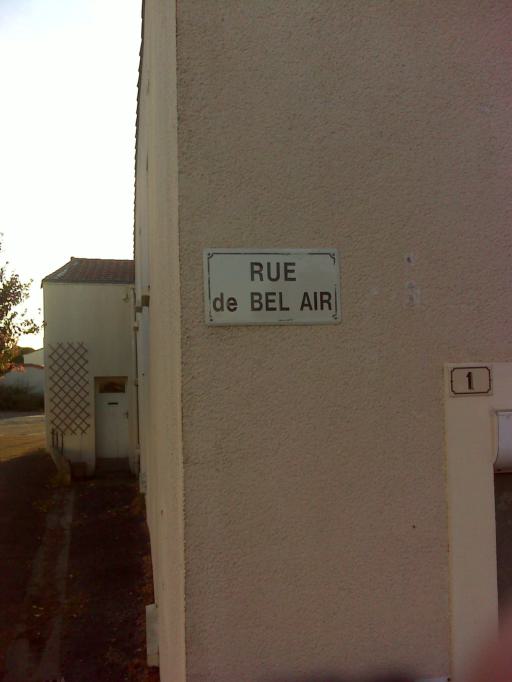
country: FR
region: Pays de la Loire
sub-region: Departement de Maine-et-Loire
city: La Chapelle-Saint-Florent
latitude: 47.3579
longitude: -1.0735
